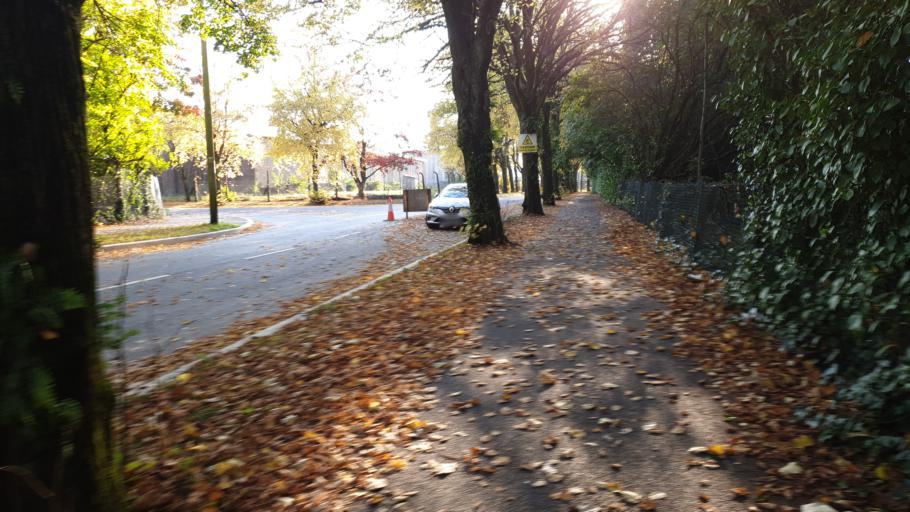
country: IE
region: Munster
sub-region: County Cork
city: Cork
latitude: 51.8993
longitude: -8.4424
